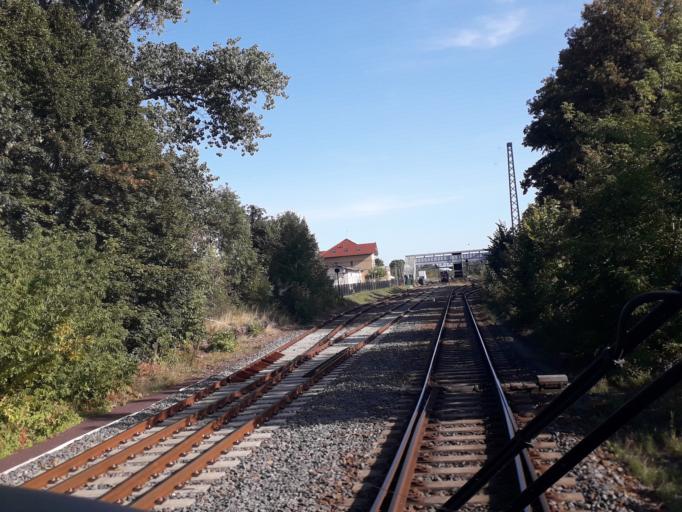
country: DE
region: Brandenburg
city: Velten
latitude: 52.6864
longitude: 13.1697
